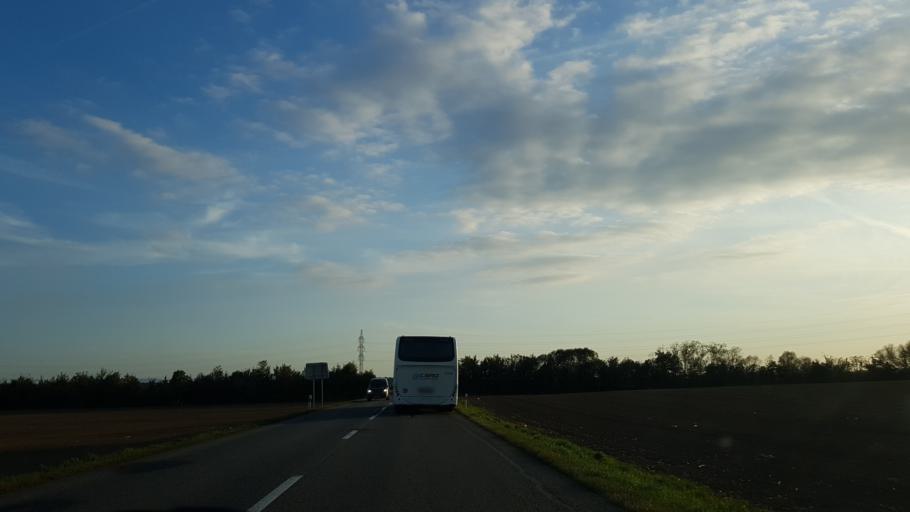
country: CZ
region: Zlin
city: Zlechov
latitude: 49.0576
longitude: 17.4036
